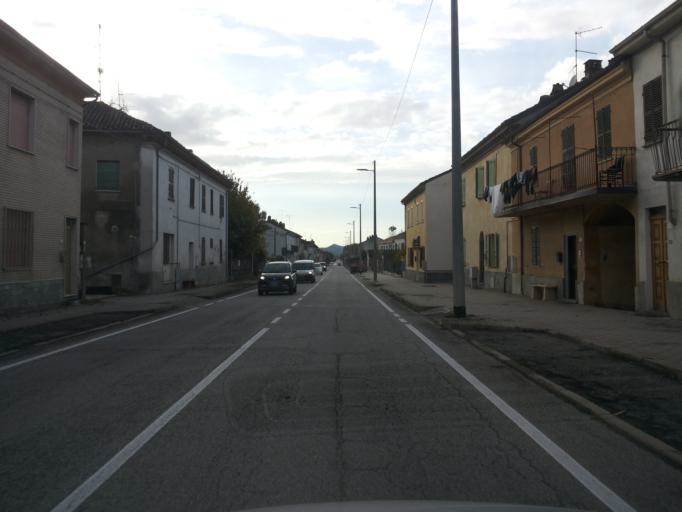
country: IT
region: Piedmont
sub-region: Provincia di Alessandria
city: Ozzano Monferrato
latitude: 45.1074
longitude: 8.3658
